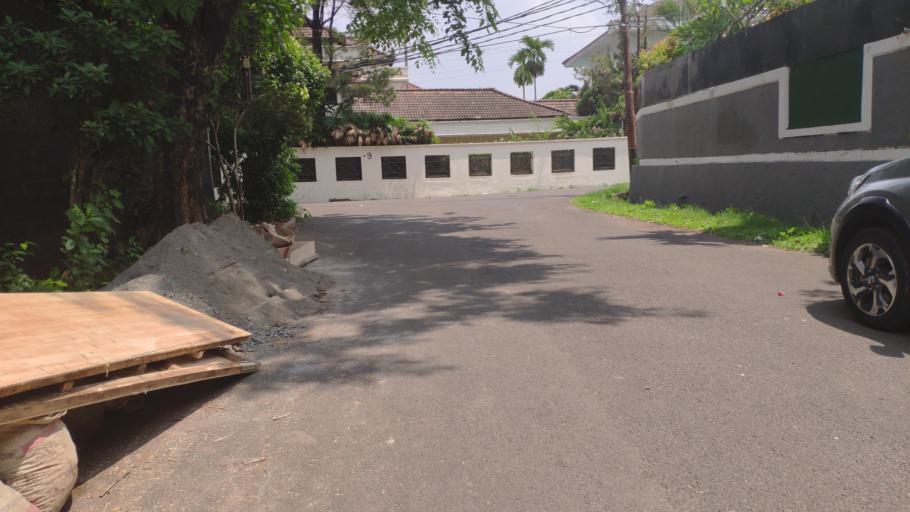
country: ID
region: Jakarta Raya
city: Jakarta
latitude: -6.2696
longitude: 106.8275
